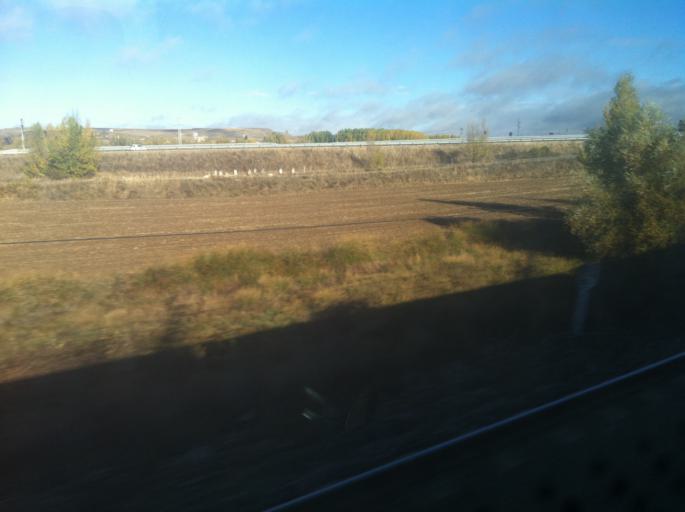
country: ES
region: Castille and Leon
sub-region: Provincia de Burgos
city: Frandovinez
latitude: 42.3005
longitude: -3.8315
